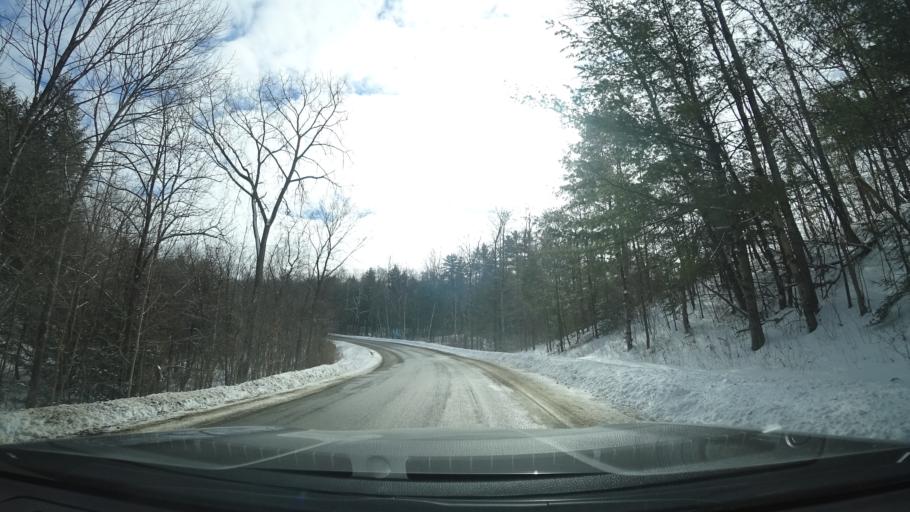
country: US
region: New York
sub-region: Washington County
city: Fort Edward
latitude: 43.2456
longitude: -73.4562
